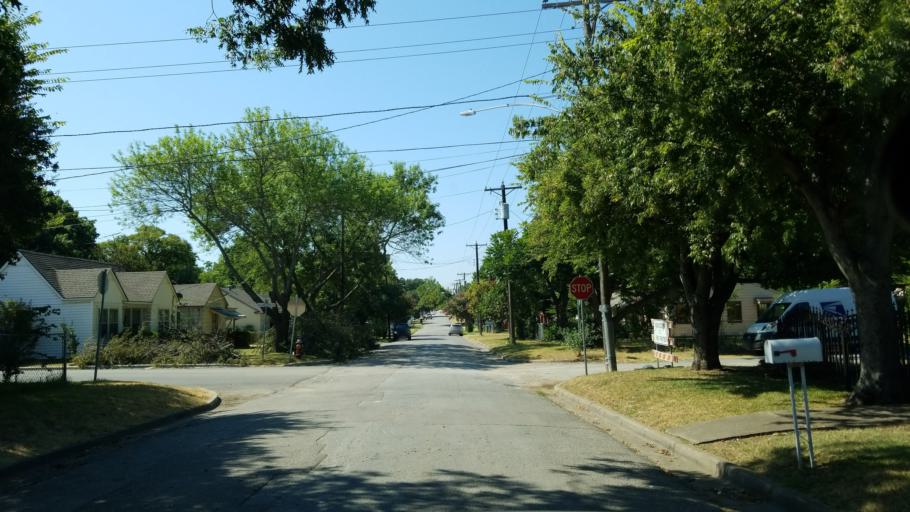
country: US
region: Texas
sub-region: Dallas County
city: Cockrell Hill
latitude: 32.7413
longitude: -96.8900
